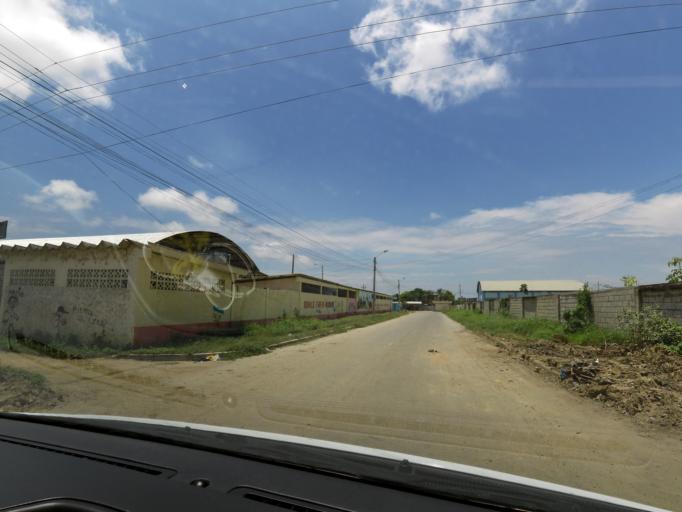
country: EC
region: El Oro
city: Huaquillas
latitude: -3.4735
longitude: -80.2367
